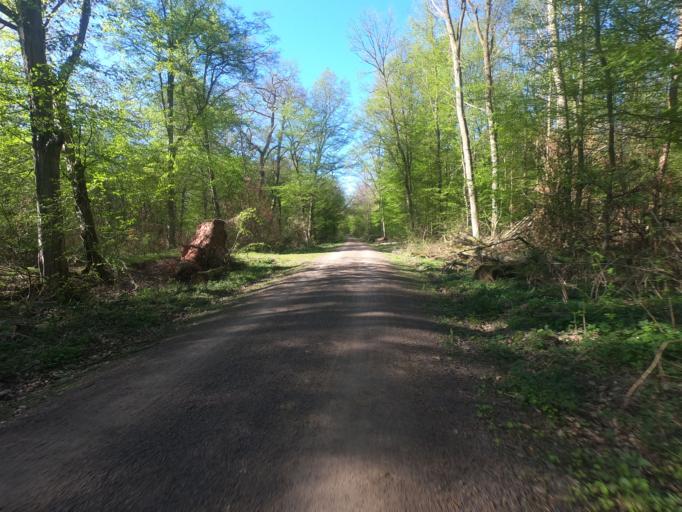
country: DE
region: Hesse
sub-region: Regierungsbezirk Darmstadt
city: Messel
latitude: 49.9520
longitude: 8.7155
